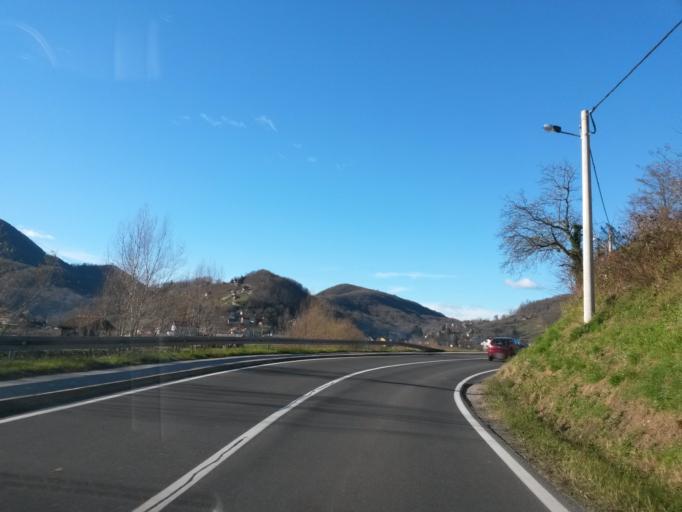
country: HR
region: Varazdinska
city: Lepoglava
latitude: 46.2070
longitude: 16.0283
